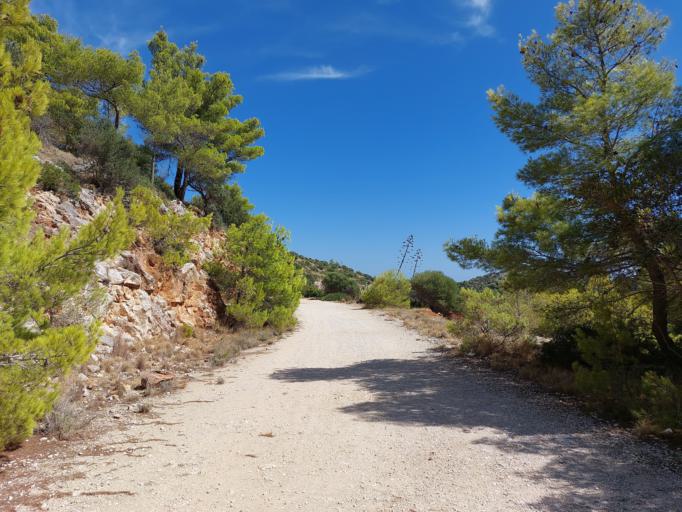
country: HR
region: Dubrovacko-Neretvanska
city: Smokvica
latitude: 42.7352
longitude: 16.8344
